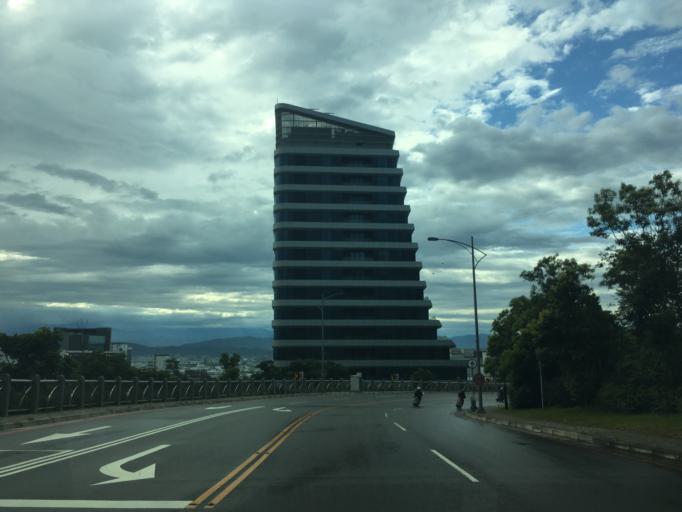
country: TW
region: Taiwan
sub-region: Taichung City
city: Taichung
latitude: 24.2101
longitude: 120.6101
